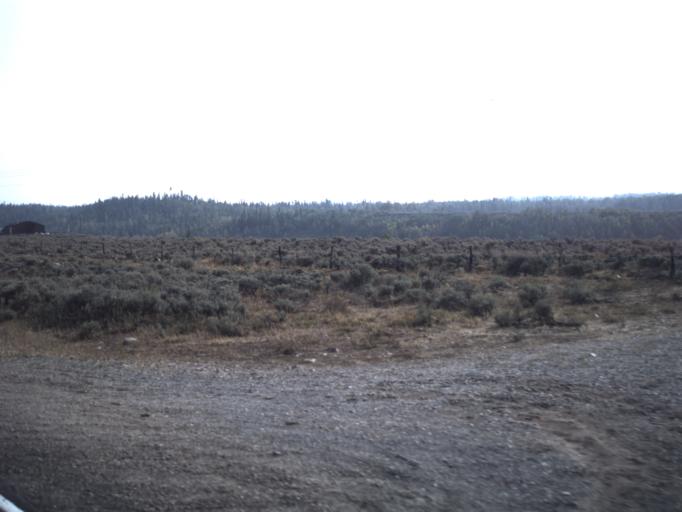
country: US
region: Wyoming
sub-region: Uinta County
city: Evanston
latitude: 40.9487
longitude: -110.8403
